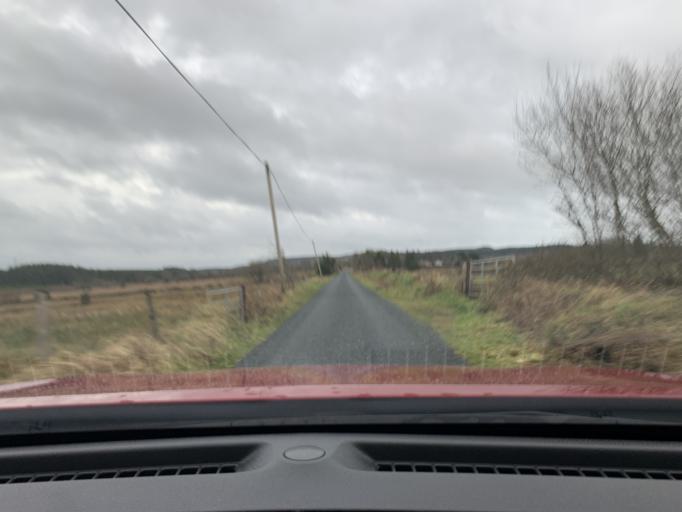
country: IE
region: Connaught
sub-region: Roscommon
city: Ballaghaderreen
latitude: 53.9697
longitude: -8.5236
